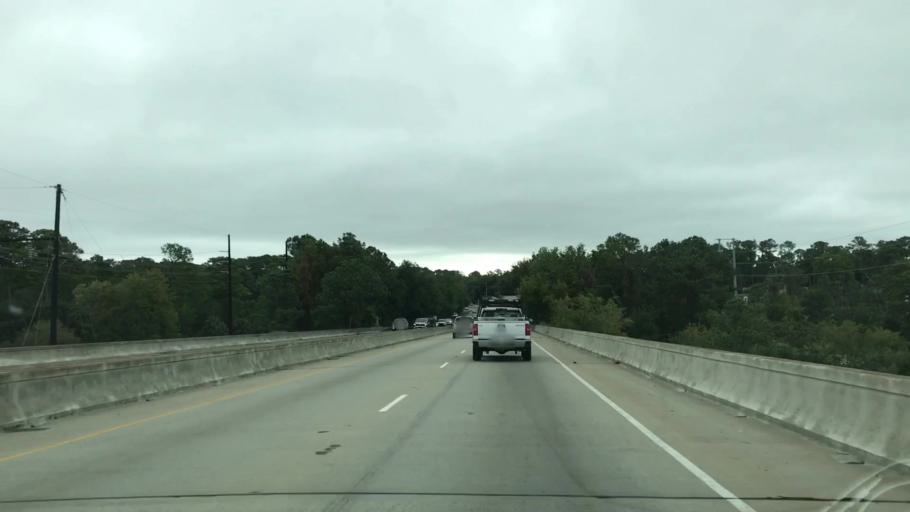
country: US
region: South Carolina
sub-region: Beaufort County
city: Hilton Head Island
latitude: 32.2227
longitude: -80.7799
